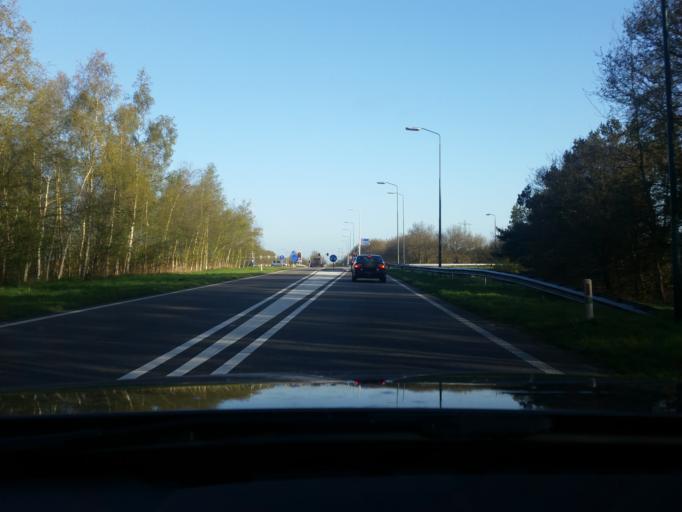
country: NL
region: North Brabant
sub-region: Gemeente Eersel
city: Eersel
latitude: 51.3701
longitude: 5.3238
